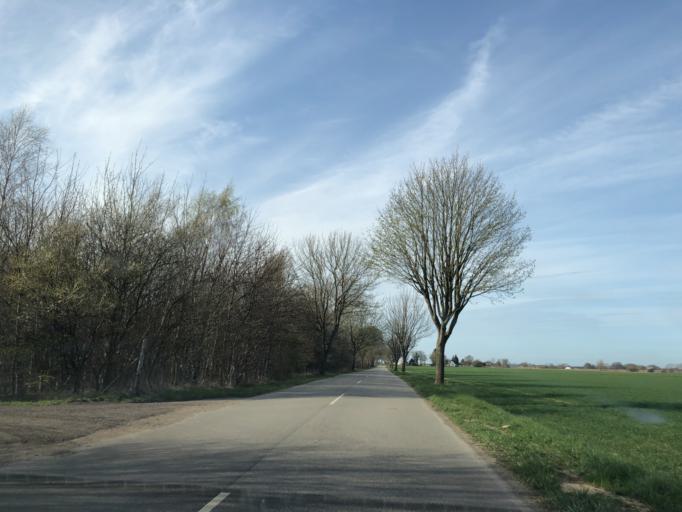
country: DK
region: Zealand
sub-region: Stevns Kommune
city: Store Heddinge
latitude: 55.3107
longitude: 12.4366
